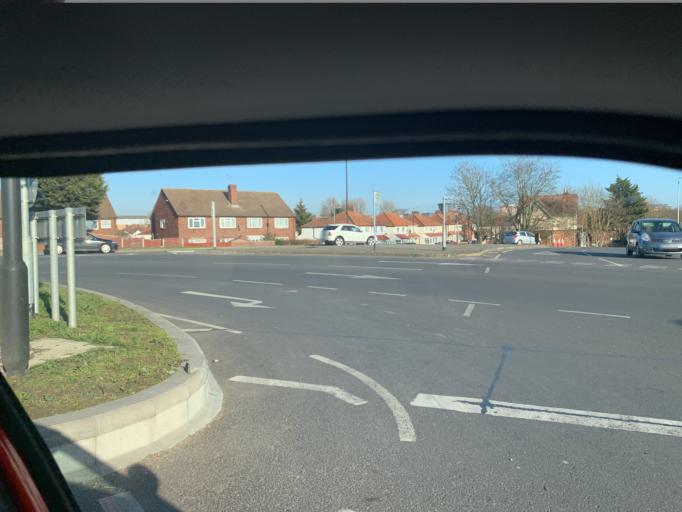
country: GB
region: England
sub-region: Slough
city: Slough
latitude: 51.5086
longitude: -0.6123
